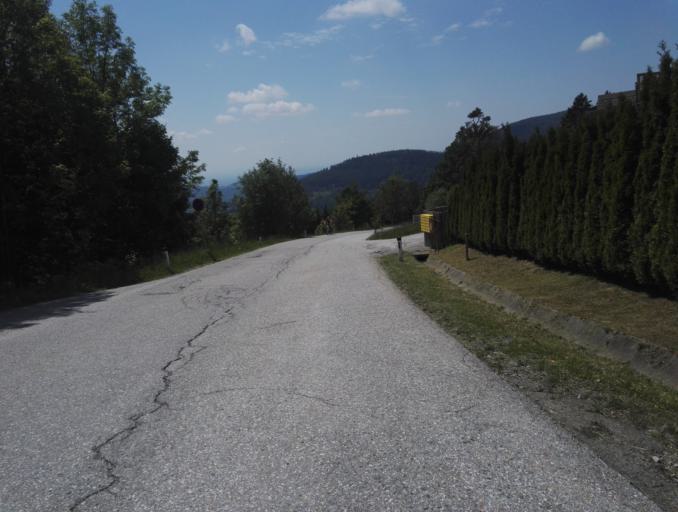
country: AT
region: Styria
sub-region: Politischer Bezirk Graz-Umgebung
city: Sankt Radegund bei Graz
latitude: 47.1931
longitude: 15.4847
